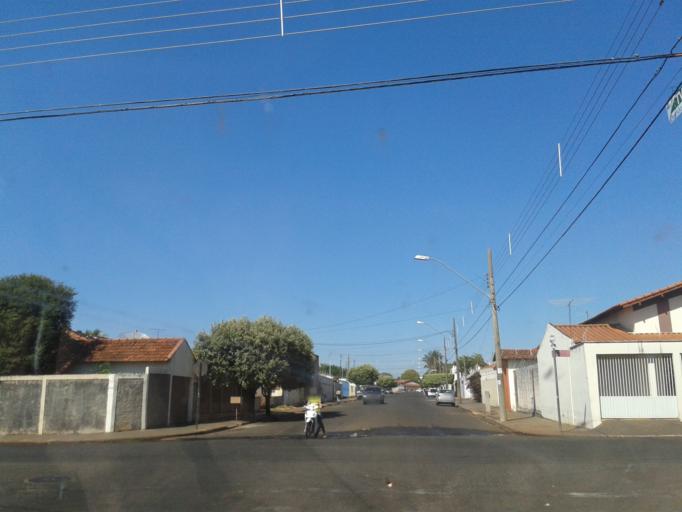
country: BR
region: Minas Gerais
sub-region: Ituiutaba
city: Ituiutaba
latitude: -18.9815
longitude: -49.4560
